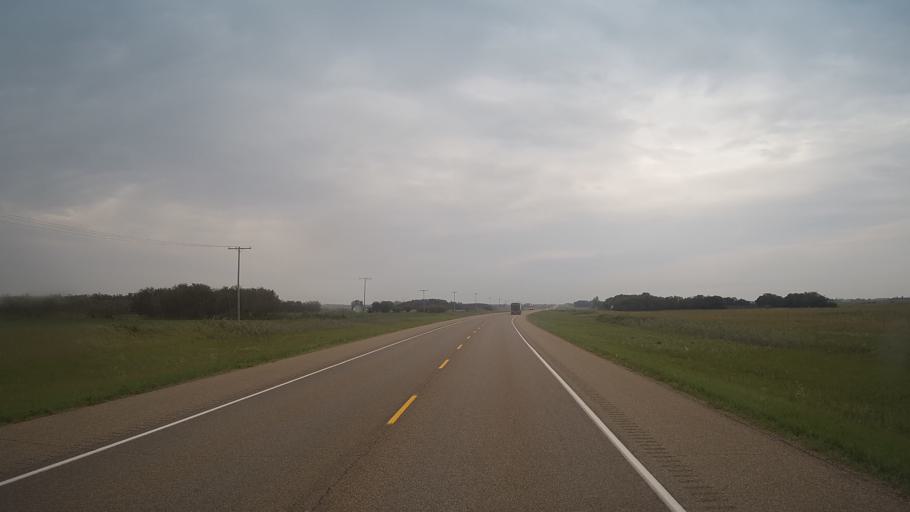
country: CA
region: Saskatchewan
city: Langham
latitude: 52.1290
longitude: -107.1118
